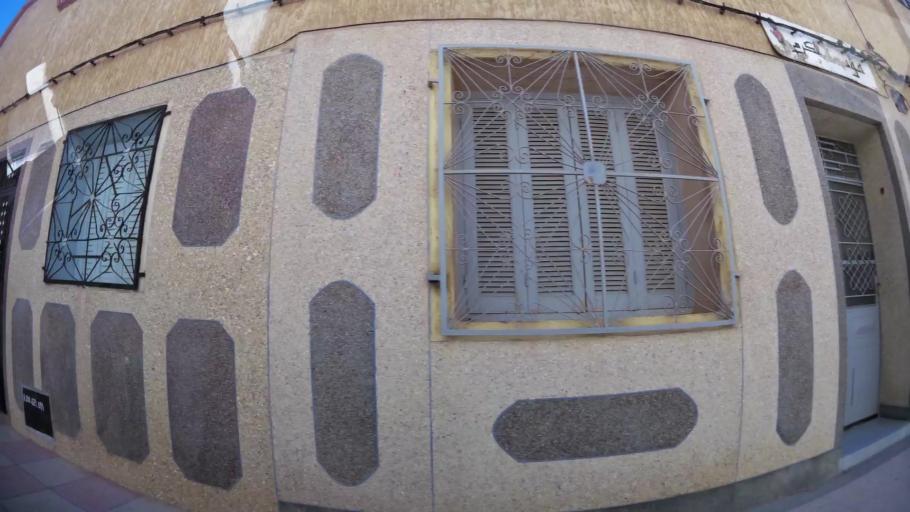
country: MA
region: Oriental
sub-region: Oujda-Angad
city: Oujda
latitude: 34.6675
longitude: -1.9288
